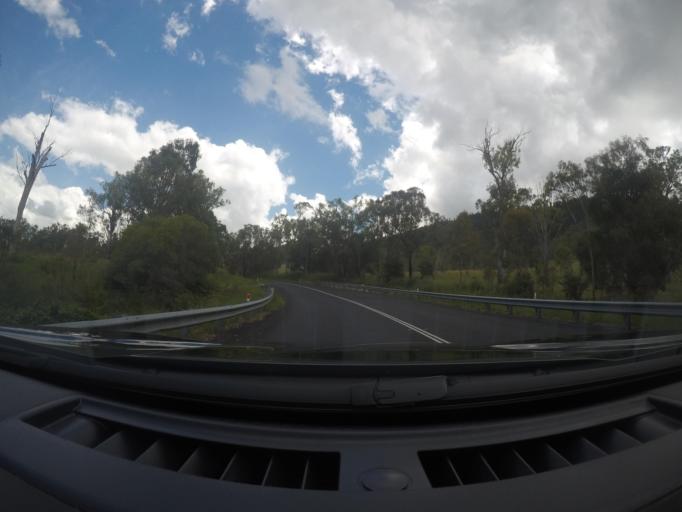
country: AU
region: Queensland
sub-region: Moreton Bay
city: Woodford
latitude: -27.0788
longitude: 152.5609
